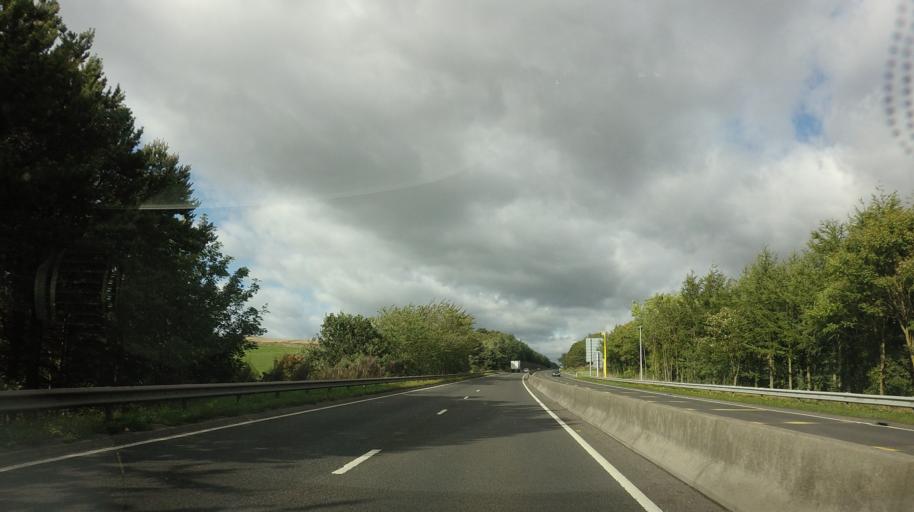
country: GB
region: Scotland
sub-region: Dundee City
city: Dundee
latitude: 56.4976
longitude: -2.9501
